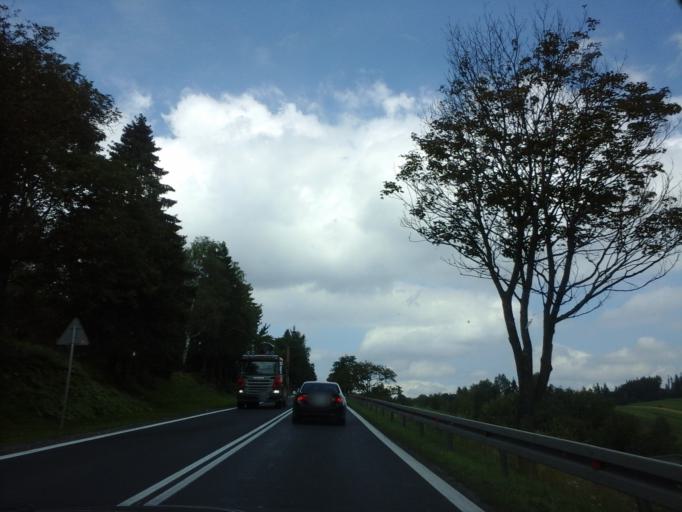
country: PL
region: Lesser Poland Voivodeship
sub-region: Powiat nowotarski
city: Klikuszowa
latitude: 49.5296
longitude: 19.9767
